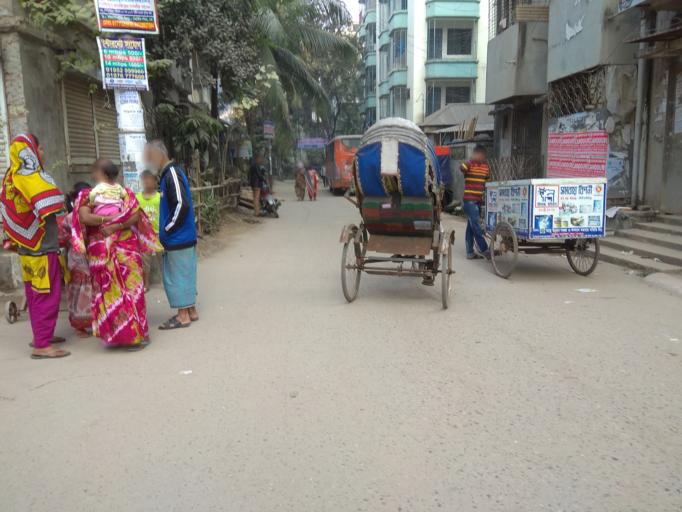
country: BD
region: Dhaka
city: Tungi
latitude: 23.8226
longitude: 90.3676
